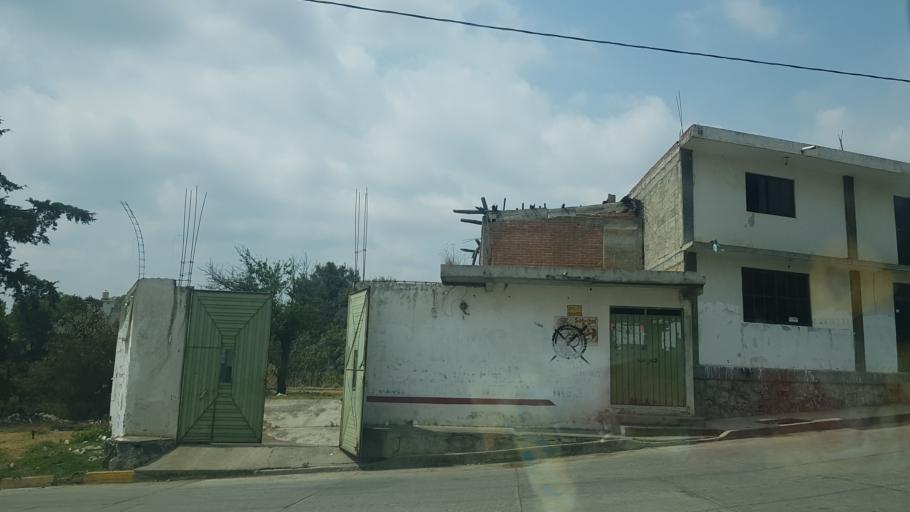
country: MX
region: Puebla
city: Domingo Arenas
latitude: 19.1356
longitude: -98.4983
